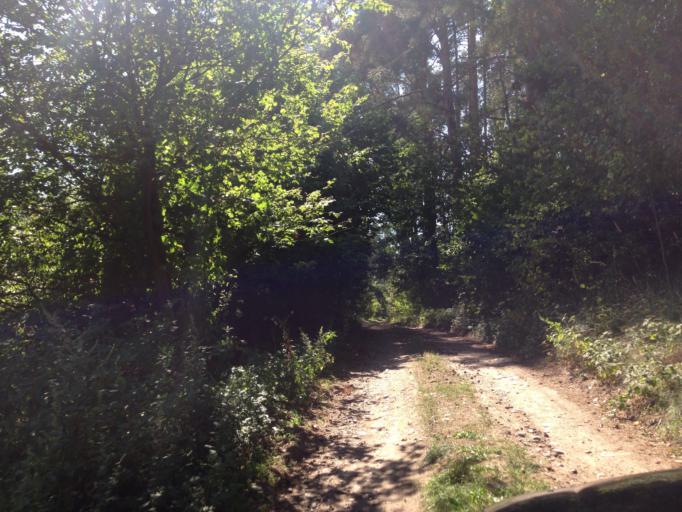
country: PL
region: Kujawsko-Pomorskie
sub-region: Powiat brodnicki
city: Bartniczka
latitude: 53.2763
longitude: 19.5722
